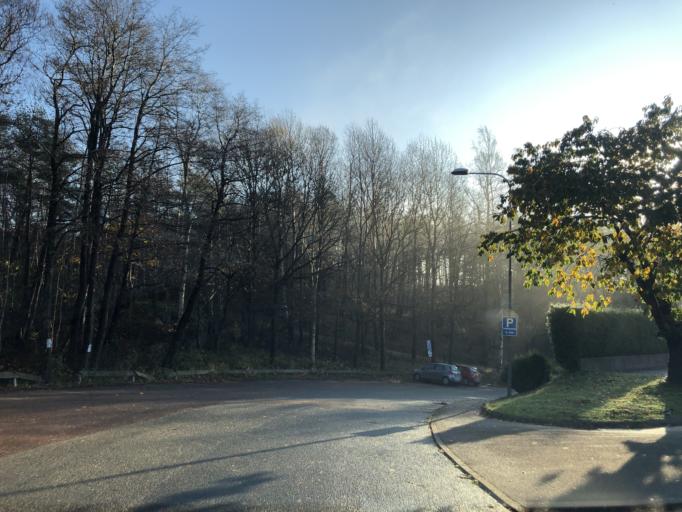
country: SE
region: Vaestra Goetaland
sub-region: Goteborg
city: Rannebergen
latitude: 57.8003
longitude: 12.0578
